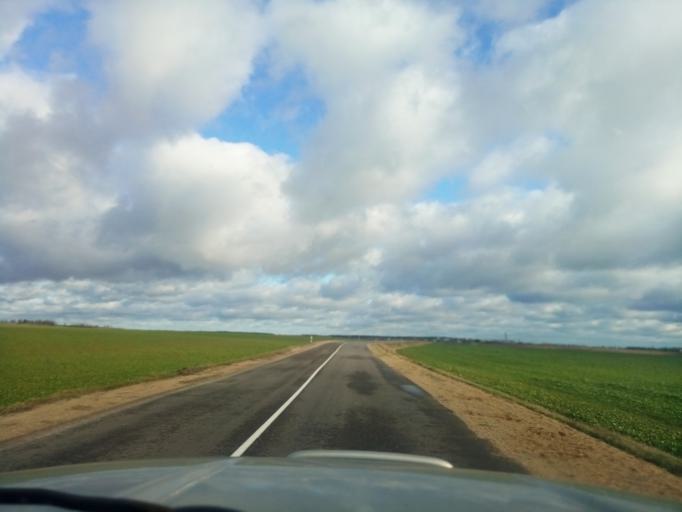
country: BY
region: Minsk
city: Kapyl'
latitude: 53.1470
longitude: 27.0457
